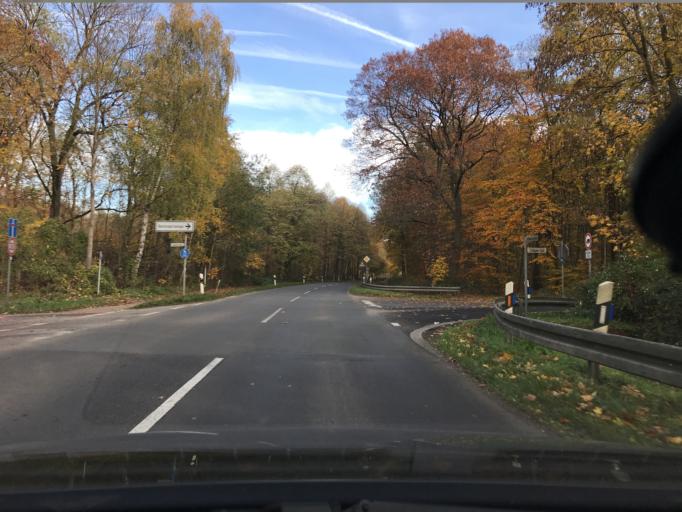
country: DE
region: North Rhine-Westphalia
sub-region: Regierungsbezirk Dusseldorf
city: Krefeld
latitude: 51.3610
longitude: 6.5434
